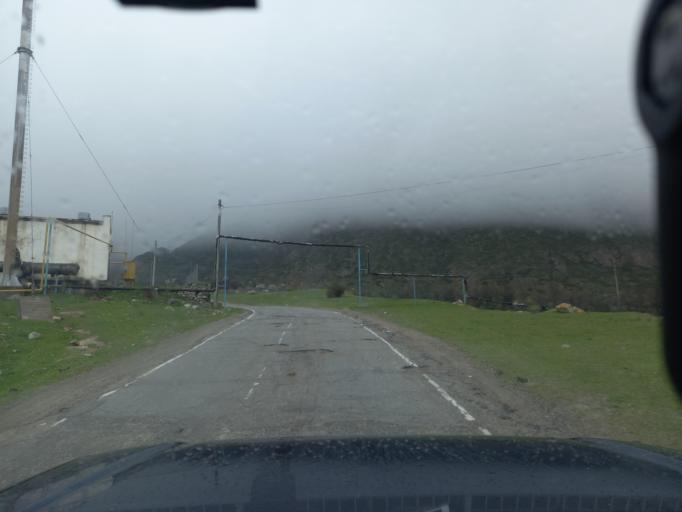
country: RU
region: Kabardino-Balkariya
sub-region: El'brusskiy Rayon
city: El'brus
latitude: 43.2787
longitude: 42.6906
